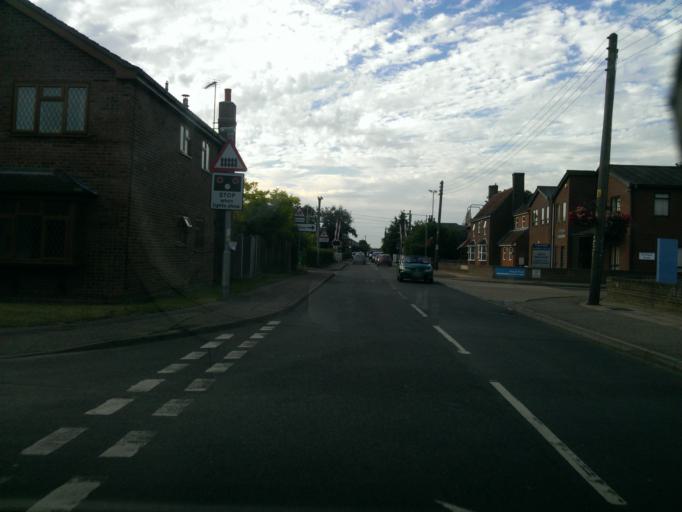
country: GB
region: England
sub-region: Essex
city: Great Bentley
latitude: 51.8507
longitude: 1.0653
